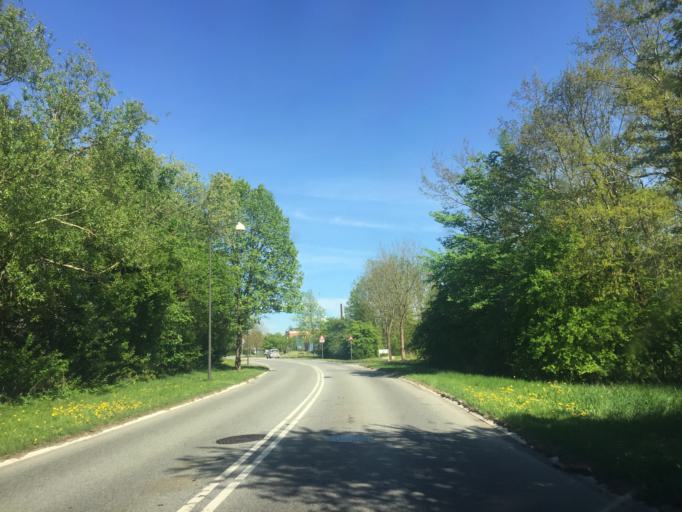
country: DK
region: Capital Region
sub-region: Herlev Kommune
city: Herlev
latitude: 55.7464
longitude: 12.4103
